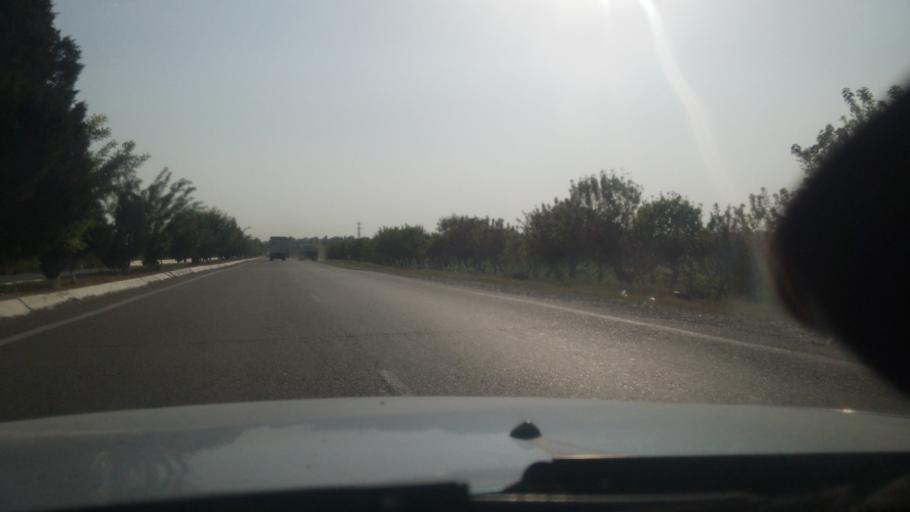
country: UZ
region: Toshkent
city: Zafar
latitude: 41.0253
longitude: 68.8594
